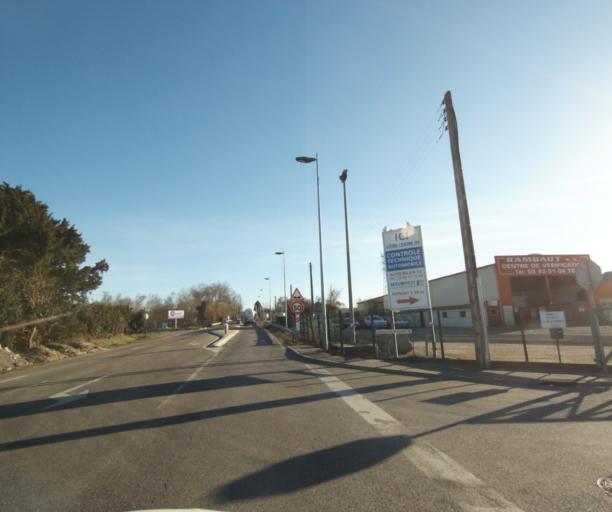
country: FR
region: Lorraine
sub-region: Departement de Meurthe-et-Moselle
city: Art-sur-Meurthe
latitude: 48.6422
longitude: 6.2535
